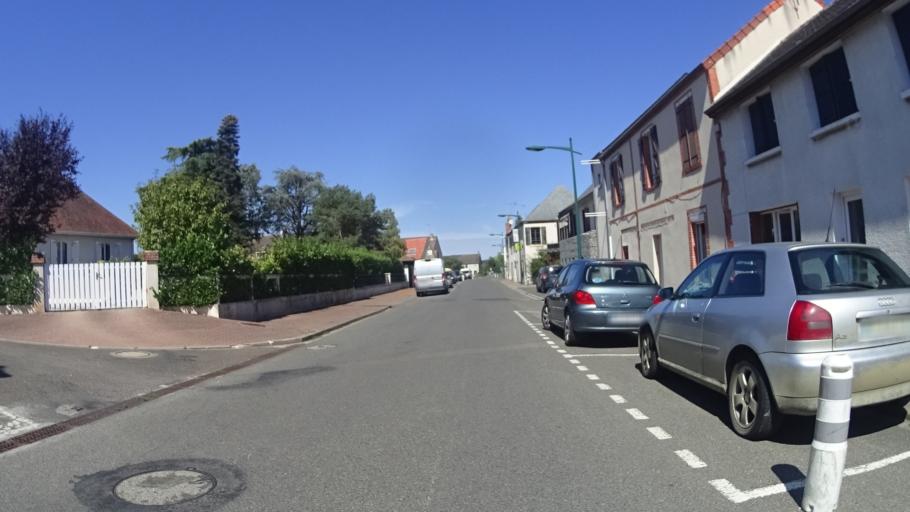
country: FR
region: Centre
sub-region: Departement du Cher
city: Belleville-sur-Loire
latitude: 47.5078
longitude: 2.8513
